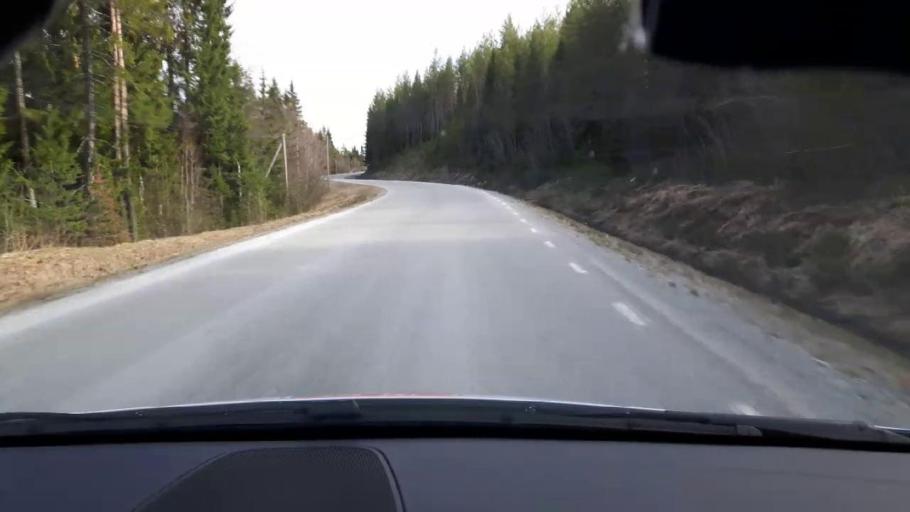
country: SE
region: Jaemtland
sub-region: Bergs Kommun
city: Hoverberg
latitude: 62.7427
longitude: 14.5826
